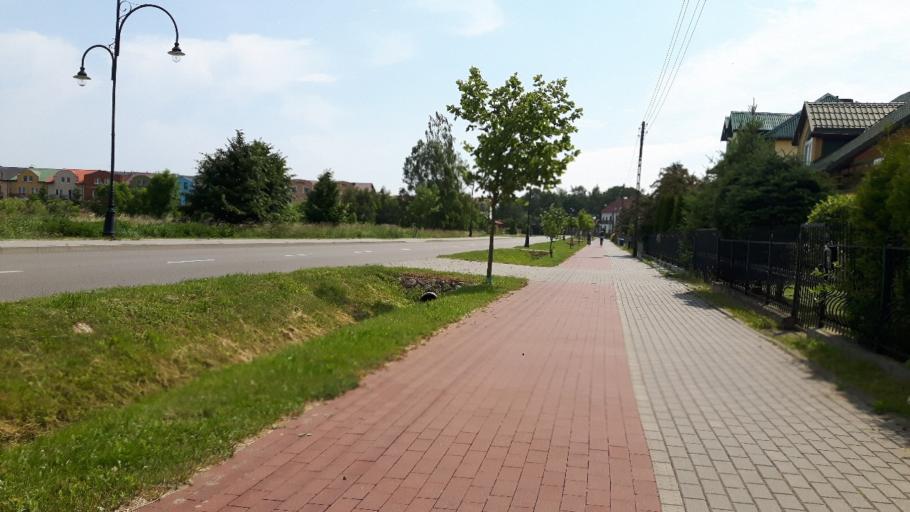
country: PL
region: Pomeranian Voivodeship
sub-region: Powiat leborski
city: Leba
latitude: 54.7500
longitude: 17.5692
